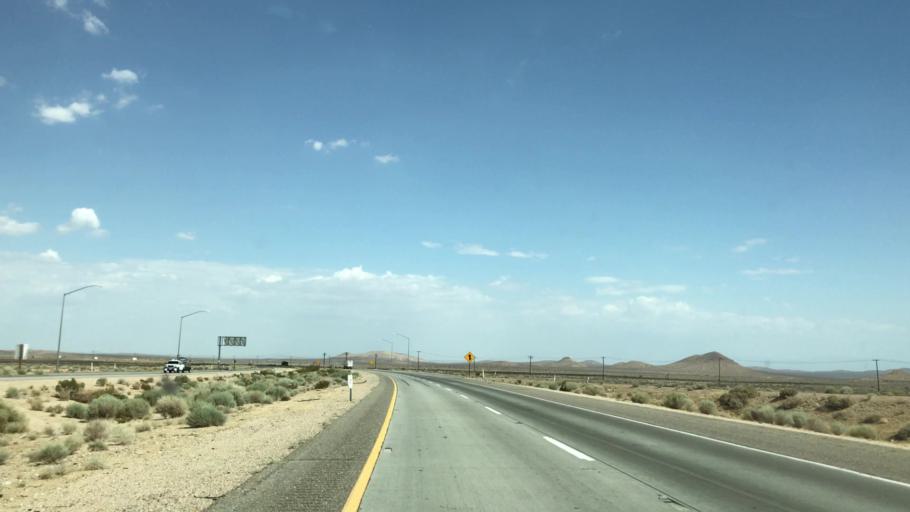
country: US
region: California
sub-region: Kern County
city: Mojave
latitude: 35.0353
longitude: -118.1043
